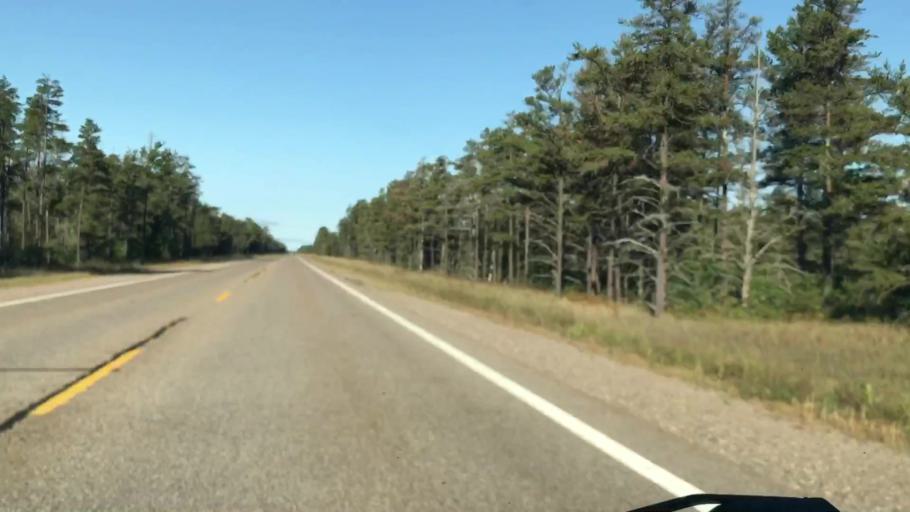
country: US
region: Michigan
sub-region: Mackinac County
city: Saint Ignace
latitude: 46.3586
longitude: -84.8352
